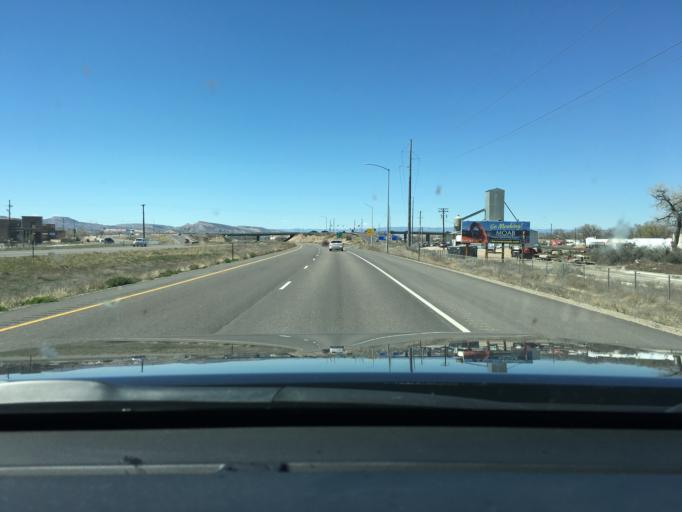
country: US
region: Colorado
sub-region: Mesa County
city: Fruita
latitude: 39.1534
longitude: -108.7315
